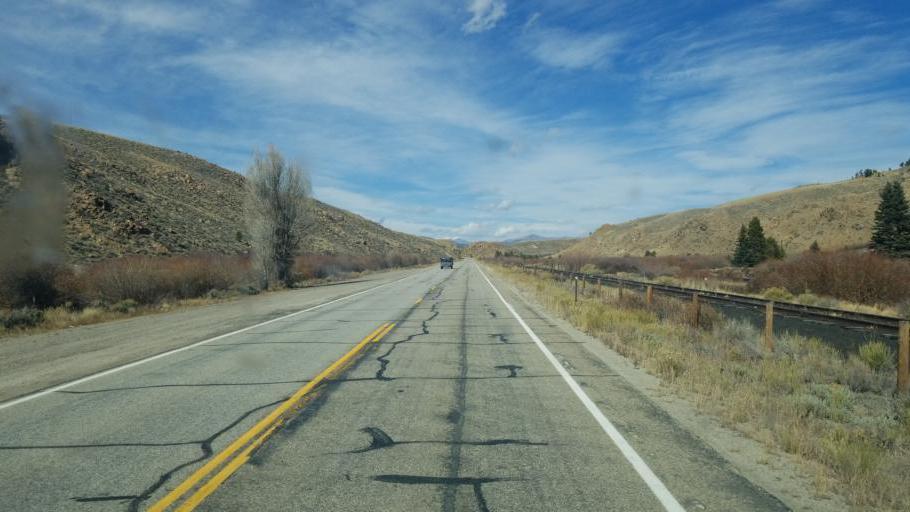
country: US
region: Colorado
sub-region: Lake County
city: Leadville
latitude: 39.0955
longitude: -106.2898
